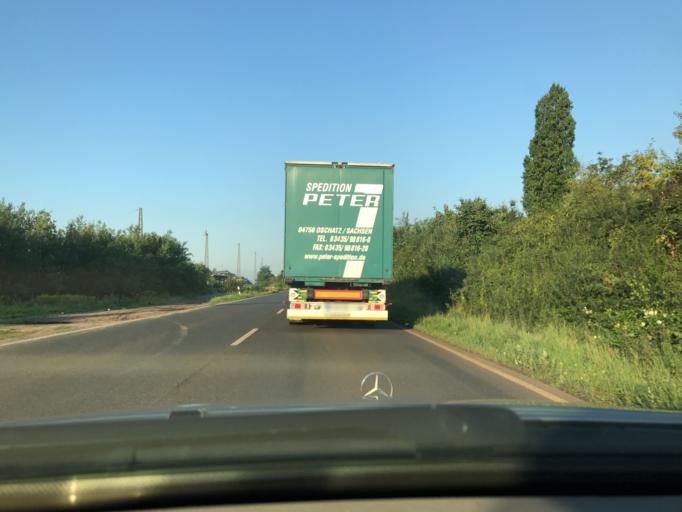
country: DE
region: North Rhine-Westphalia
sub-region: Regierungsbezirk Dusseldorf
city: Hochfeld
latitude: 51.3950
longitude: 6.7086
